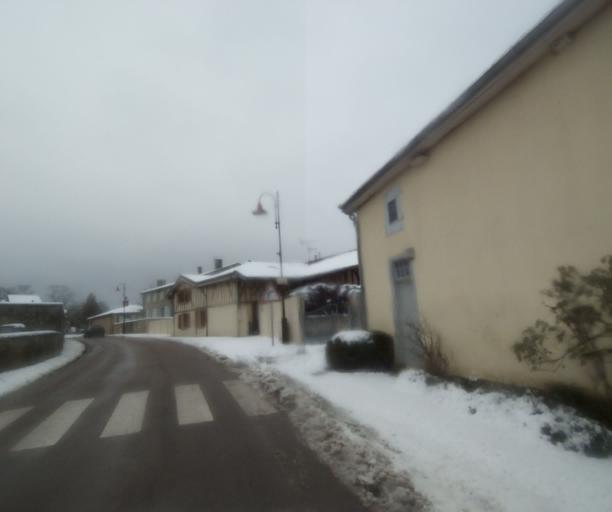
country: FR
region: Champagne-Ardenne
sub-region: Departement de la Haute-Marne
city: Laneuville-a-Remy
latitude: 48.5047
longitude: 4.8689
